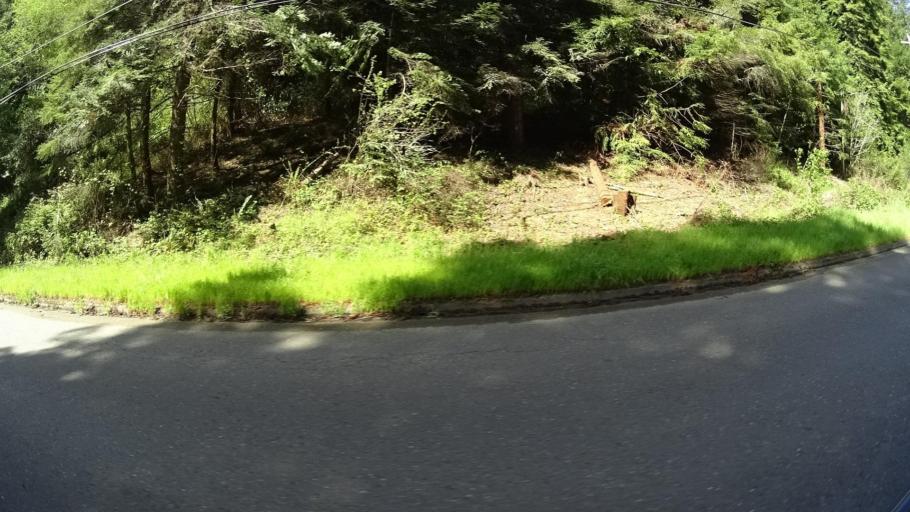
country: US
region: California
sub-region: Humboldt County
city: Hydesville
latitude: 40.5693
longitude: -124.1119
